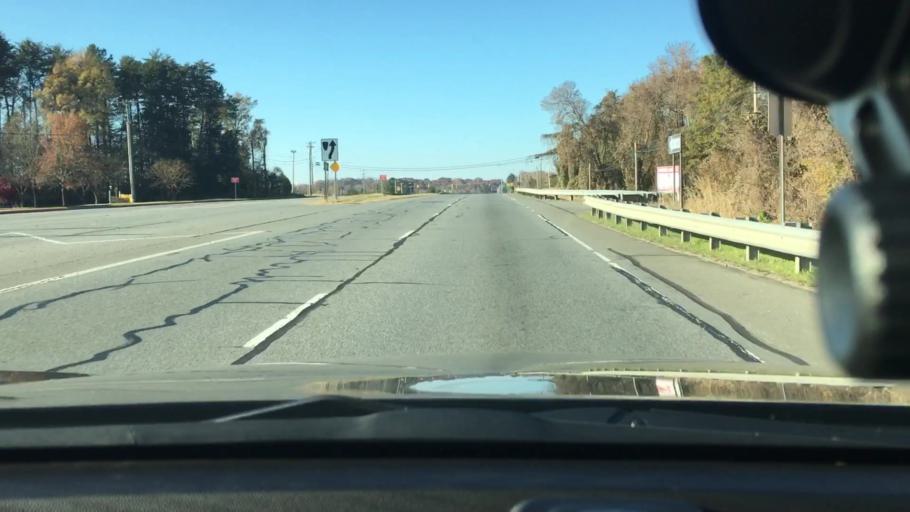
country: US
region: North Carolina
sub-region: Cabarrus County
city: Concord
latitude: 35.3662
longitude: -80.5809
